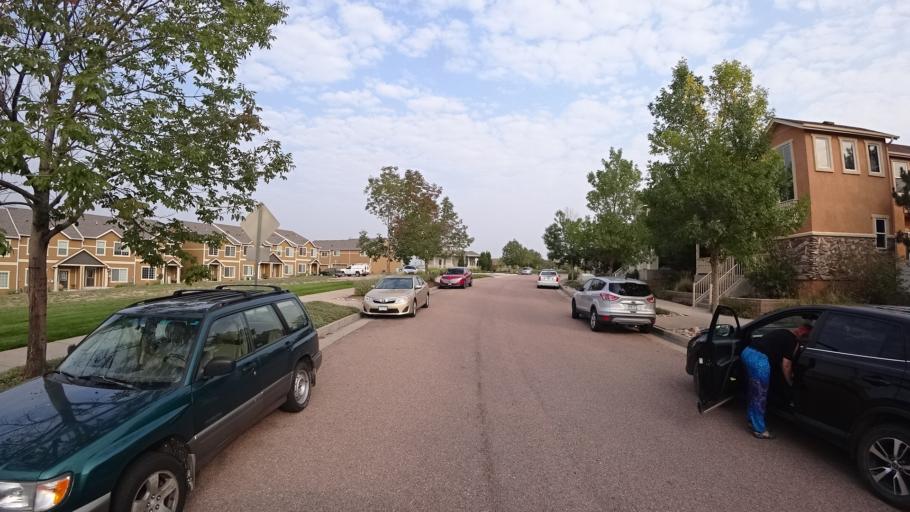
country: US
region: Colorado
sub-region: El Paso County
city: Stratmoor
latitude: 38.8070
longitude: -104.7853
